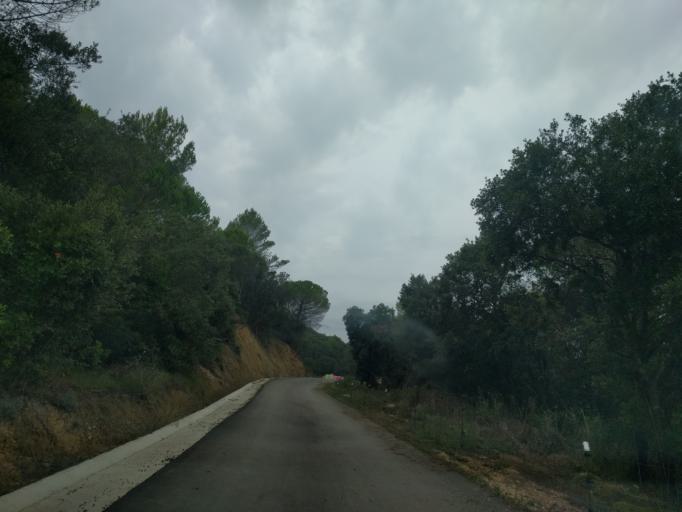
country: ES
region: Catalonia
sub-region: Provincia de Girona
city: la Cellera de Ter
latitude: 42.0179
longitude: 2.6339
